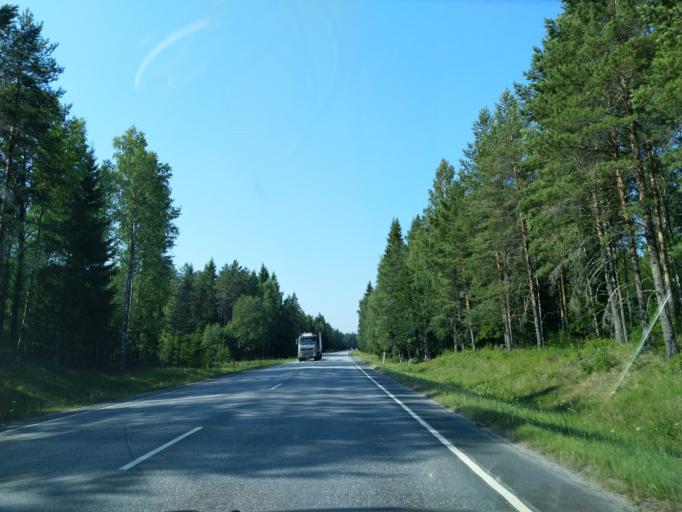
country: FI
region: Satakunta
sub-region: Pori
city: Noormarkku
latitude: 61.6304
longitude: 21.9295
